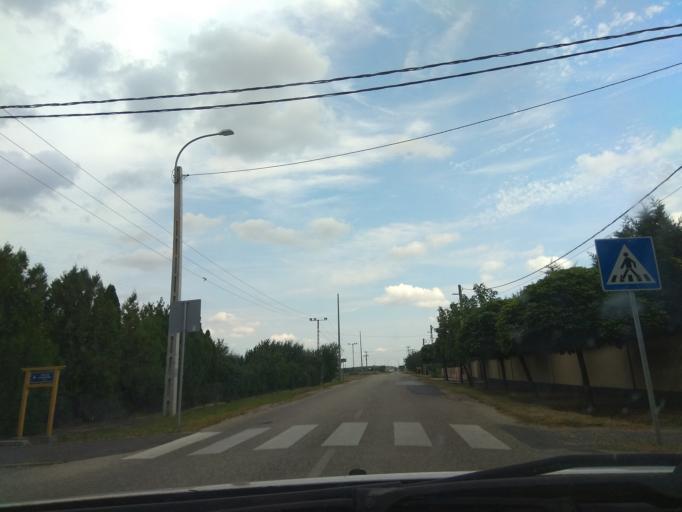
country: HU
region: Borsod-Abauj-Zemplen
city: Malyi
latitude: 48.0398
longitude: 20.8441
